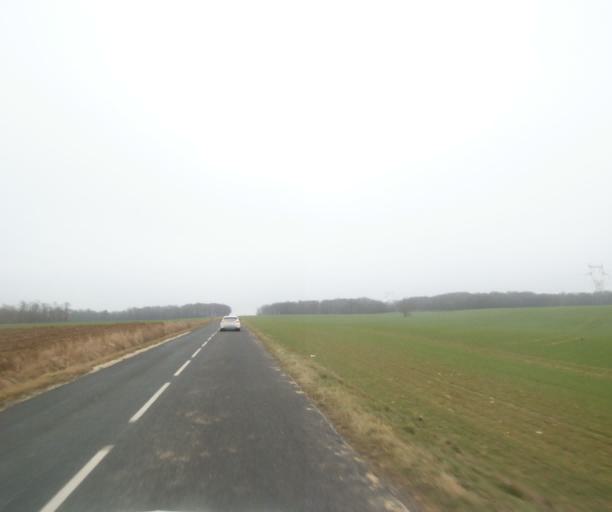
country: FR
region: Champagne-Ardenne
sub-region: Departement de la Haute-Marne
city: Bienville
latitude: 48.5213
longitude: 5.0623
